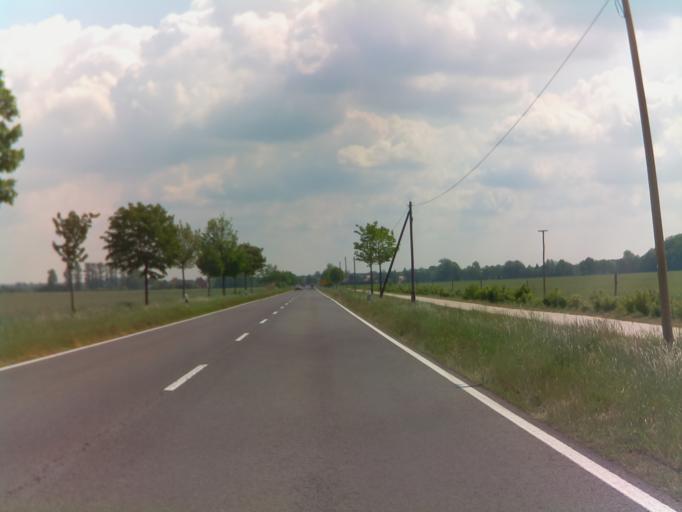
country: DE
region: Saxony-Anhalt
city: Schonhausen
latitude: 52.5526
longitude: 12.0960
